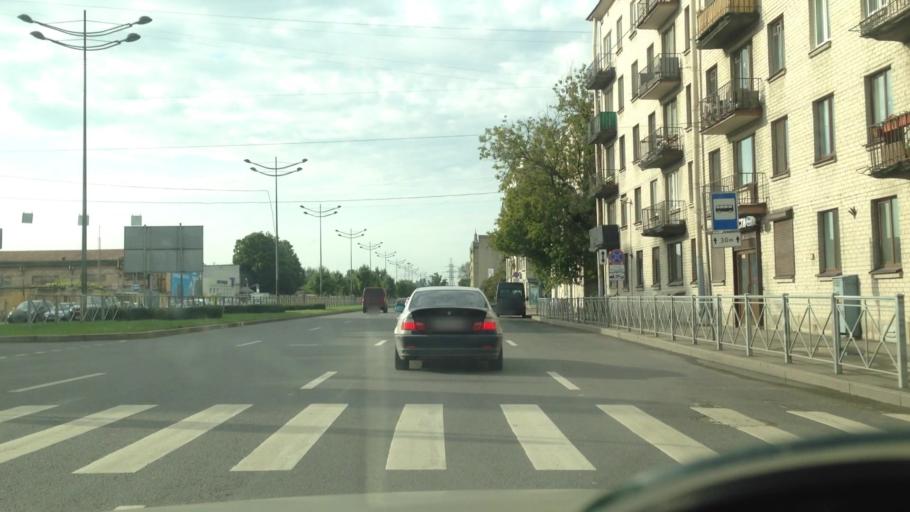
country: RU
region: St.-Petersburg
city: Centralniy
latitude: 59.9075
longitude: 30.3452
